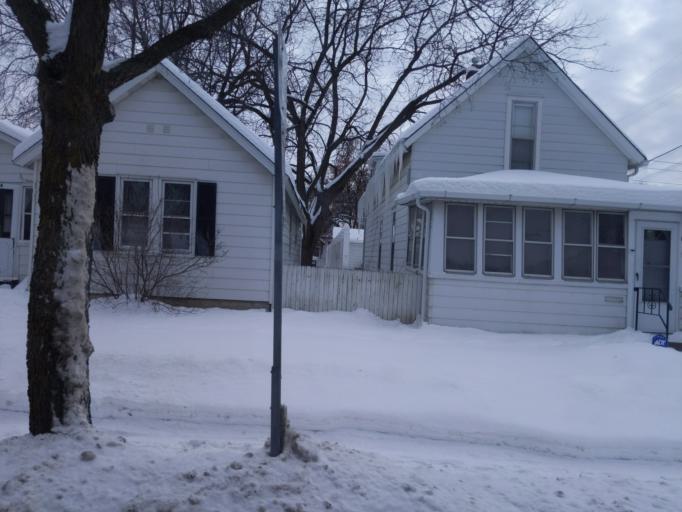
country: US
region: Minnesota
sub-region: Ramsey County
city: Saint Paul
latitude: 44.9629
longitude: -93.1287
